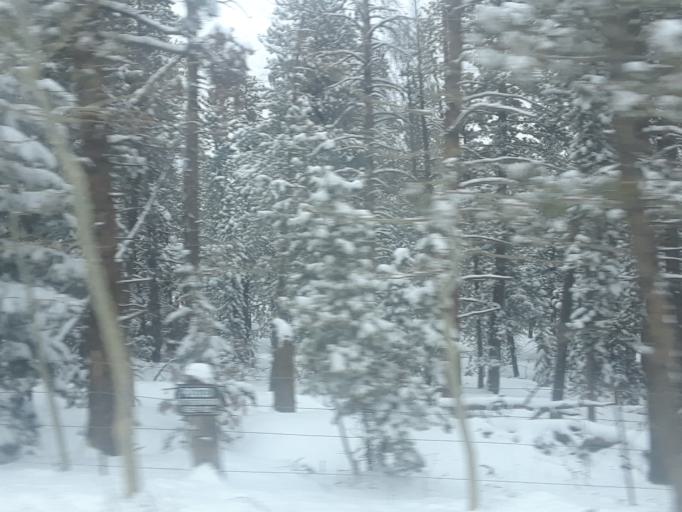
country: US
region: Colorado
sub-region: Boulder County
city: Coal Creek
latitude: 39.9253
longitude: -105.3887
